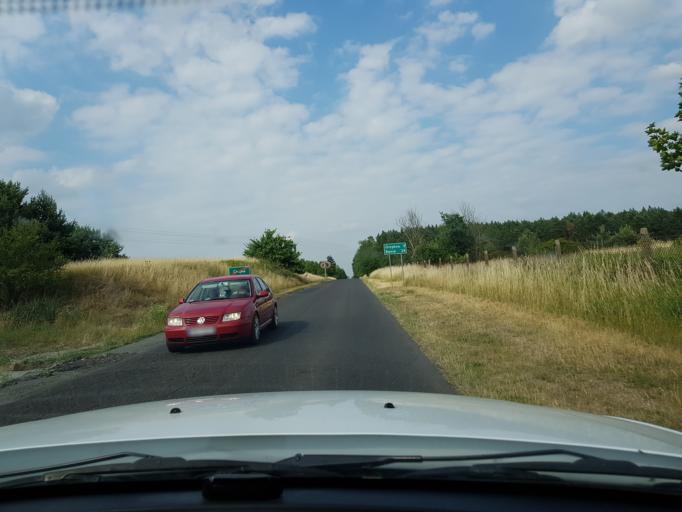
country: PL
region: West Pomeranian Voivodeship
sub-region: Powiat gryfinski
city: Chojna
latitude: 52.9679
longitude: 14.4582
